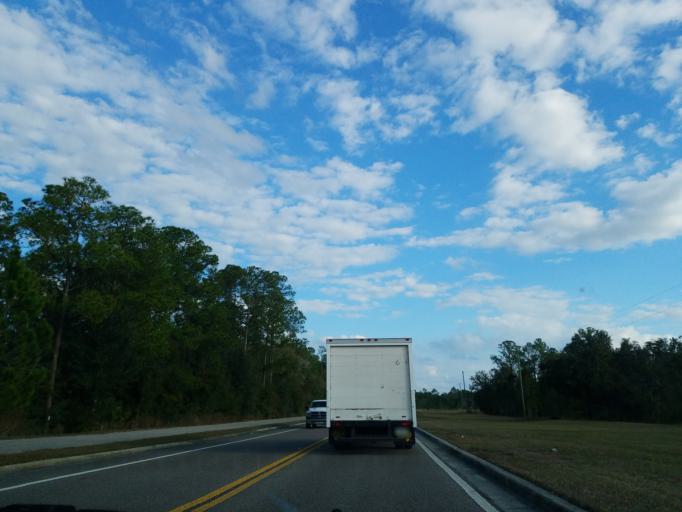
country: US
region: Florida
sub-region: Pasco County
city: Odessa
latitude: 28.2211
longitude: -82.6392
